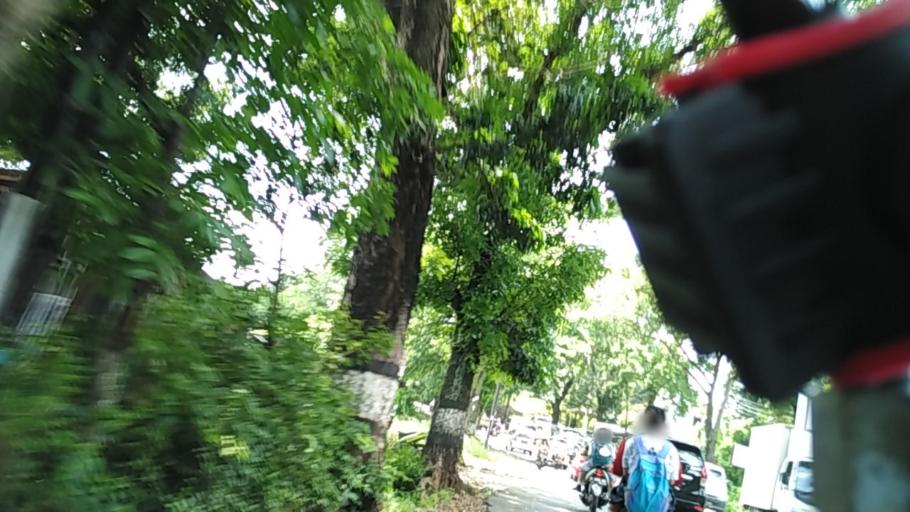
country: ID
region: Central Java
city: Semarang
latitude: -7.0012
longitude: 110.3803
